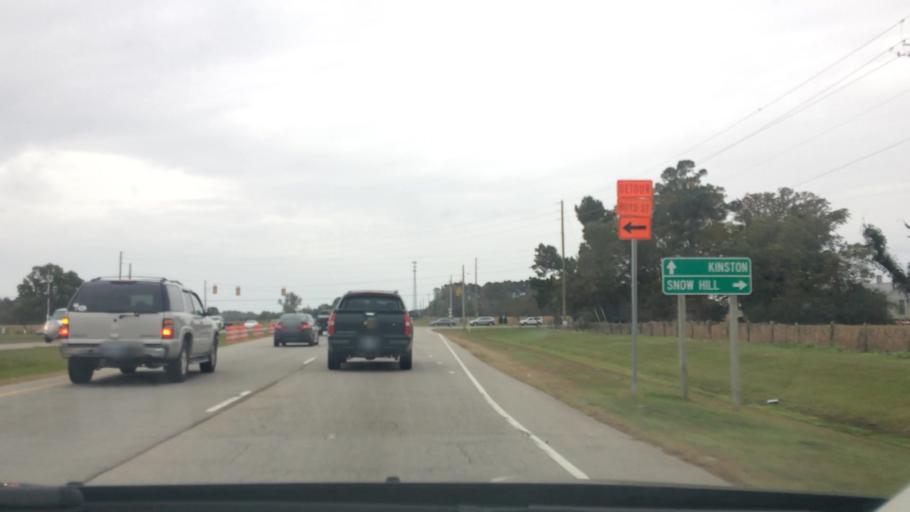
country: US
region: North Carolina
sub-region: Pitt County
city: Winterville
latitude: 35.5293
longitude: -77.4081
